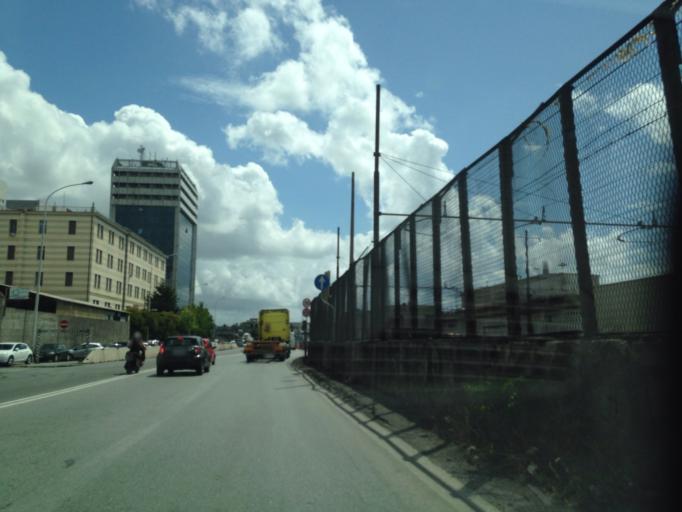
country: IT
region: Liguria
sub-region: Provincia di Genova
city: San Teodoro
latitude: 44.4081
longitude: 8.8951
